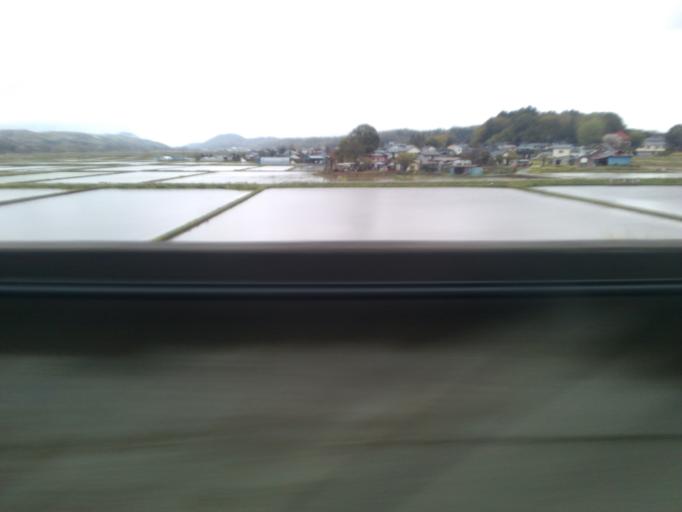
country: JP
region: Fukushima
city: Sukagawa
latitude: 37.2401
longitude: 140.2943
